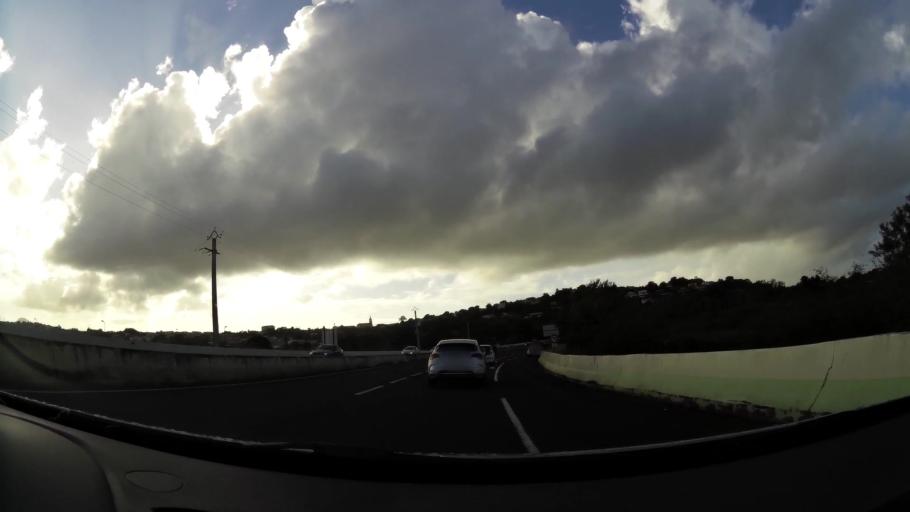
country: MQ
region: Martinique
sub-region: Martinique
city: Ducos
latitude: 14.5843
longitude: -60.9802
